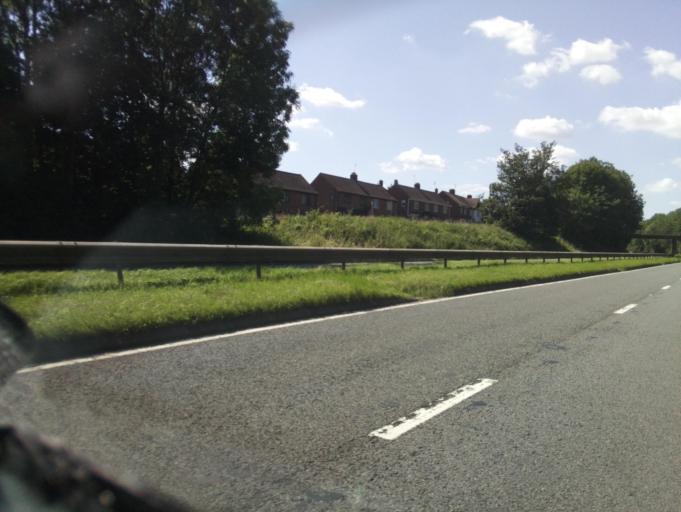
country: GB
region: England
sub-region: Warwickshire
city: Atherstone
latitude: 52.5789
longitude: -1.5385
